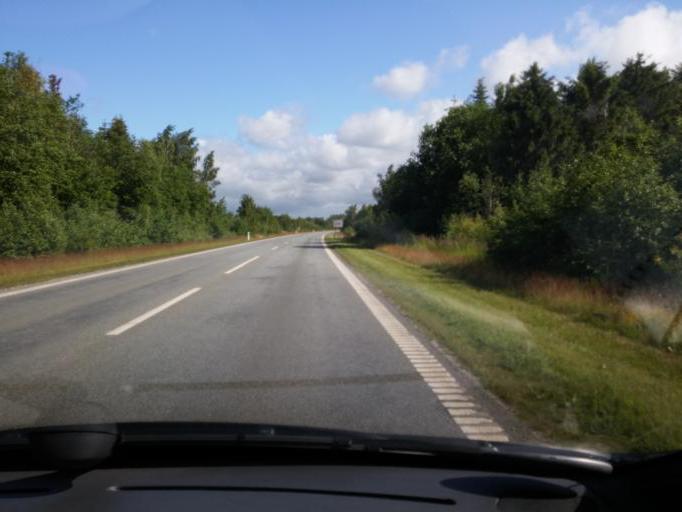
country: DK
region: Capital Region
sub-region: Hillerod Kommune
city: Hillerod
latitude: 55.9479
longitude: 12.2445
